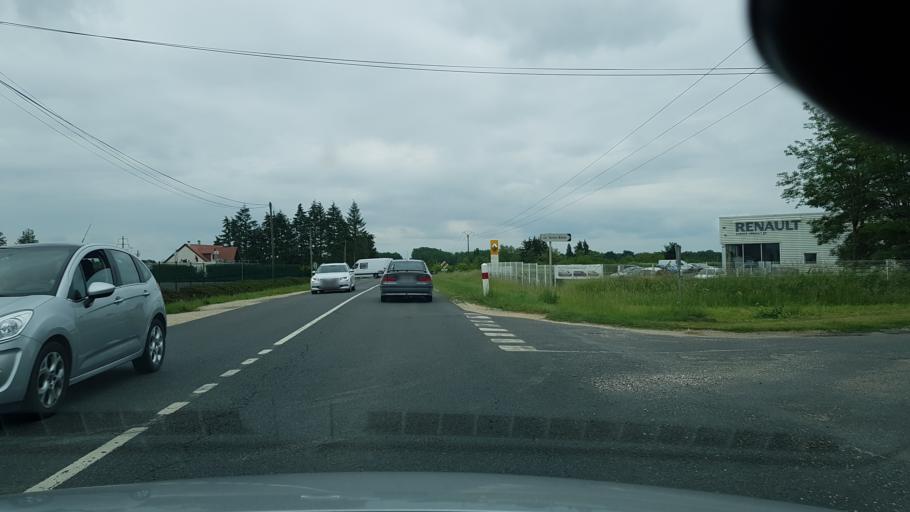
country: FR
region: Centre
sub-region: Departement du Loir-et-Cher
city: Selles-sur-Cher
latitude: 47.2927
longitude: 1.5260
